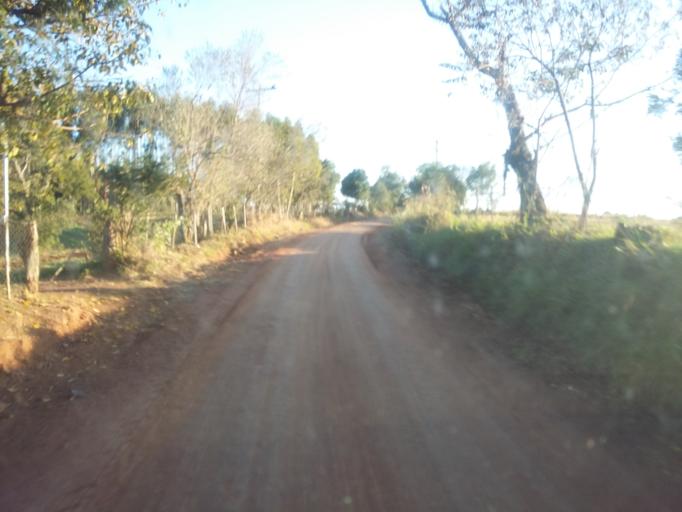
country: BR
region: Rio Grande do Sul
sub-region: Camaqua
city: Camaqua
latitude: -30.7089
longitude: -51.7673
